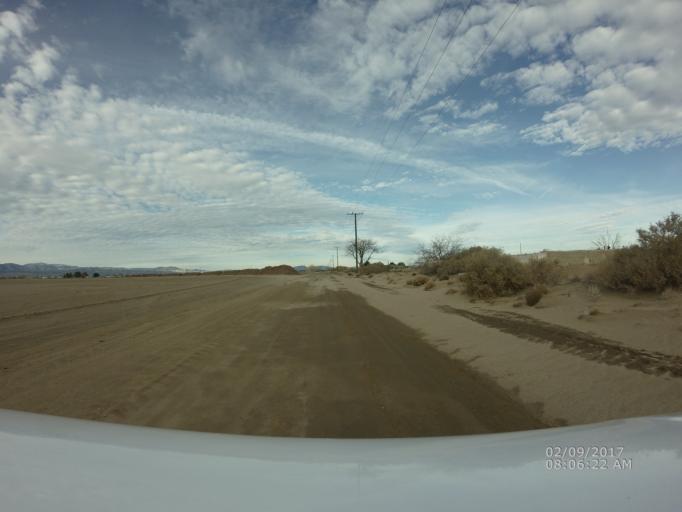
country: US
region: California
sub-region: Los Angeles County
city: Lake Los Angeles
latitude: 34.5726
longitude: -117.8494
